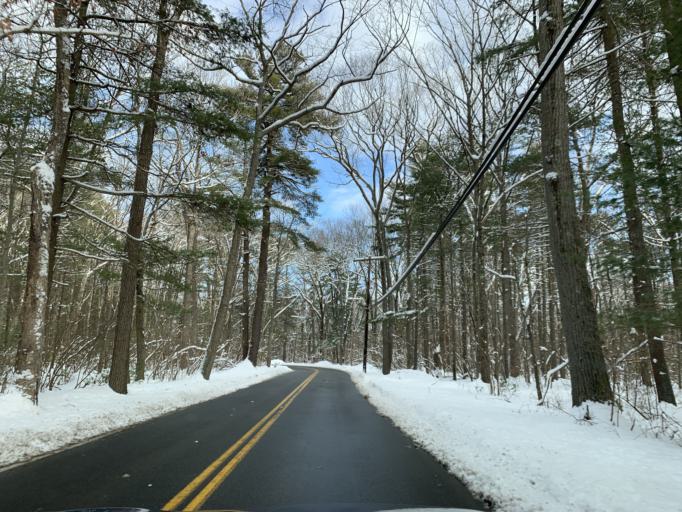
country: US
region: Massachusetts
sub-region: Norfolk County
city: Dover
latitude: 42.2588
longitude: -71.2784
